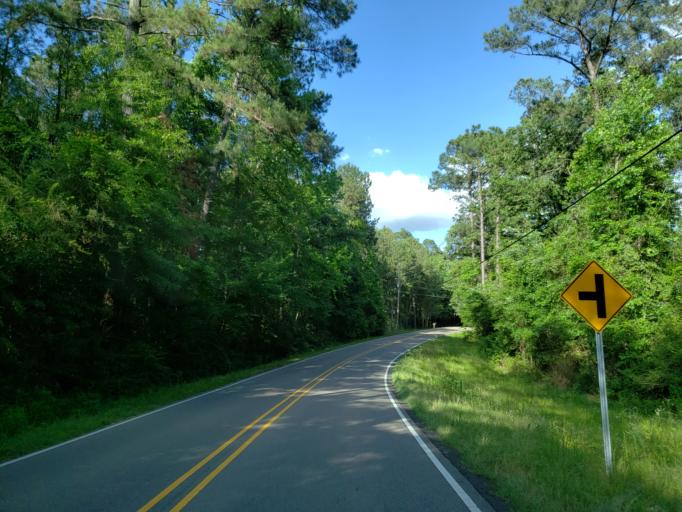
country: US
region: Mississippi
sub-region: Lamar County
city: West Hattiesburg
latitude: 31.2725
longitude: -89.4039
